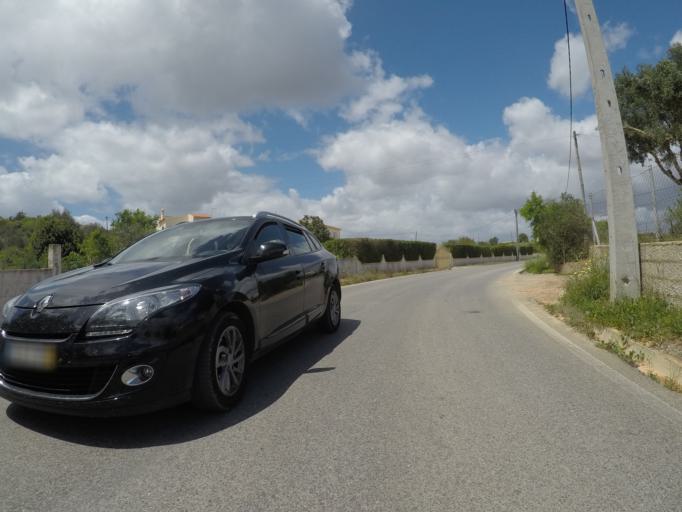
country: PT
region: Faro
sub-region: Lagoa
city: Lagoa
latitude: 37.1168
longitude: -8.4123
